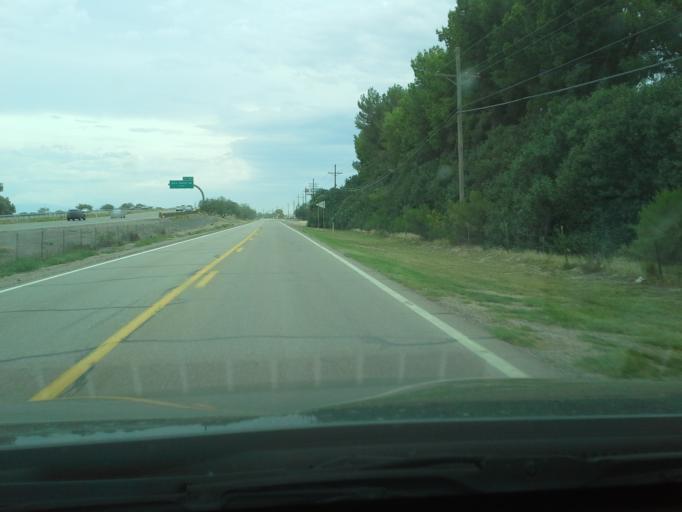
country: US
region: Arizona
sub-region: Pima County
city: Marana
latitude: 32.4118
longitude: -111.1473
